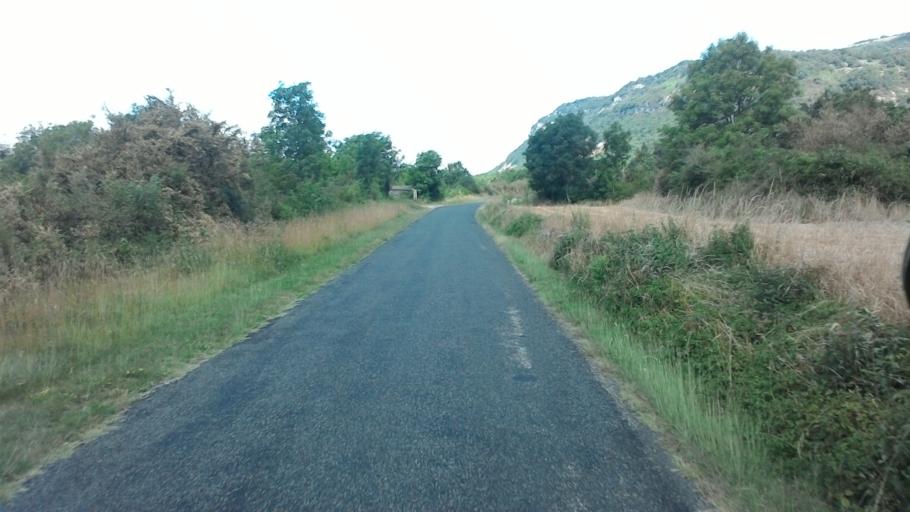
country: FR
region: Rhone-Alpes
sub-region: Departement de l'Ain
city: Sault-Brenaz
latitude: 45.8622
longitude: 5.4198
